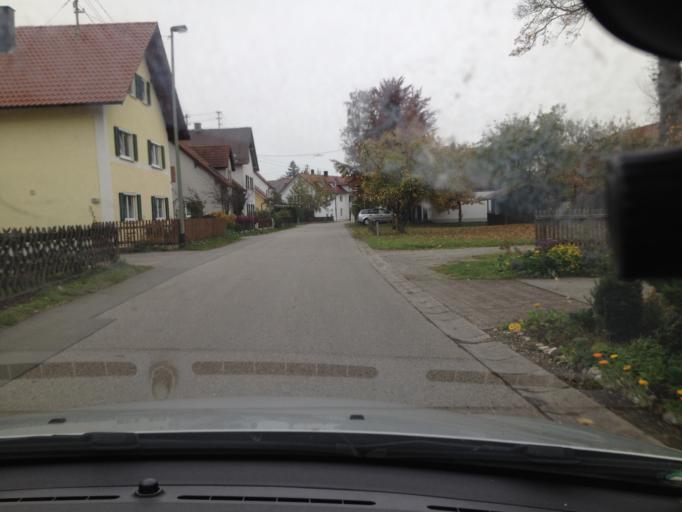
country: DE
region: Bavaria
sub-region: Swabia
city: Ettringen
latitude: 48.1063
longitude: 10.6549
